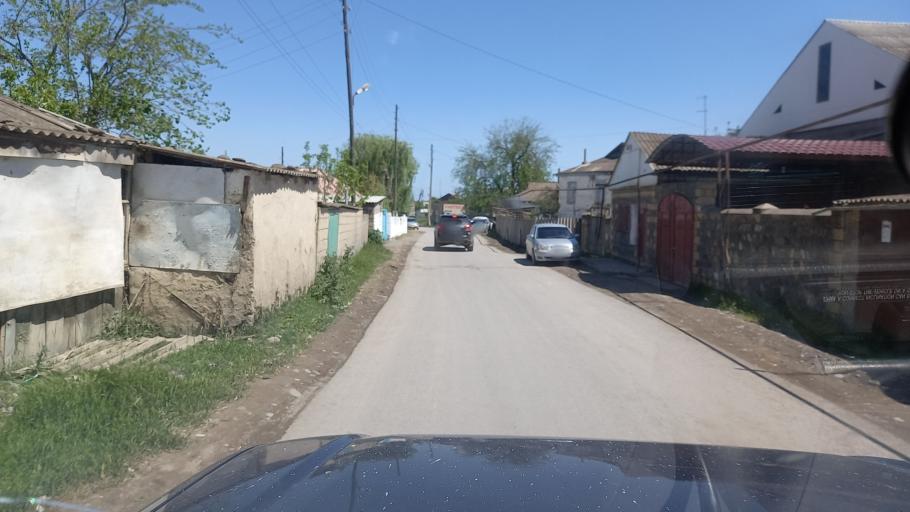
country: RU
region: Dagestan
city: Samur
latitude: 41.8146
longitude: 48.5043
